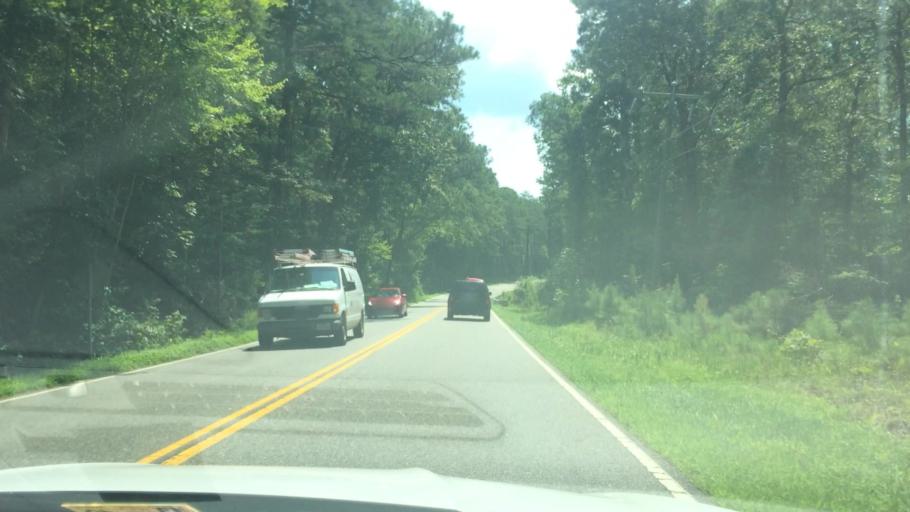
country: US
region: Virginia
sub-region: James City County
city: Williamsburg
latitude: 37.3156
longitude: -76.7803
